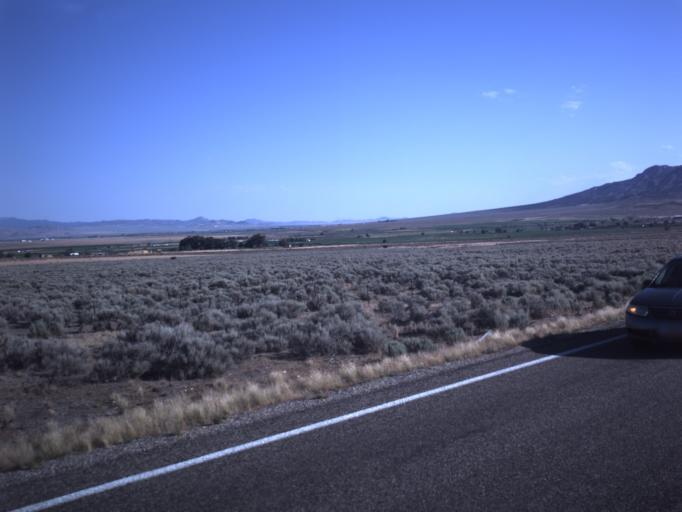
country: US
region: Utah
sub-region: Beaver County
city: Milford
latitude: 38.1909
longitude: -112.9373
